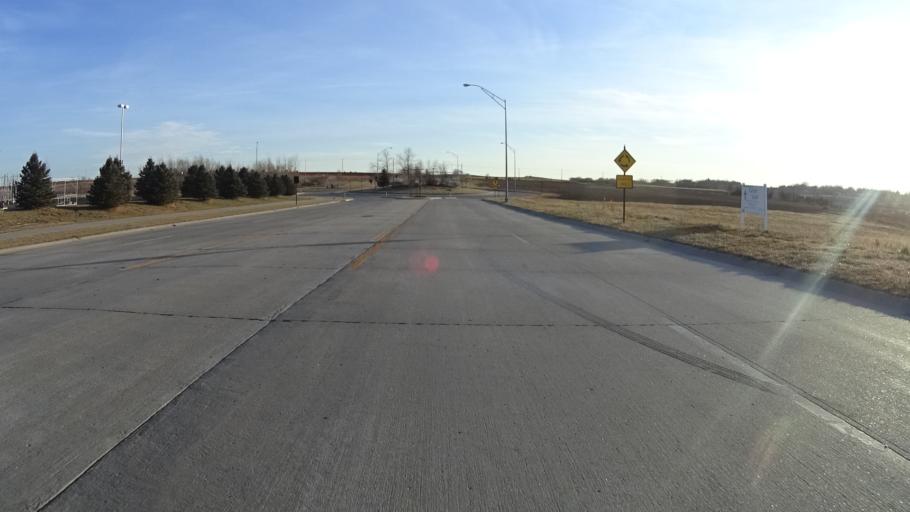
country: US
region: Nebraska
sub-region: Sarpy County
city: Chalco
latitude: 41.1512
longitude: -96.1100
